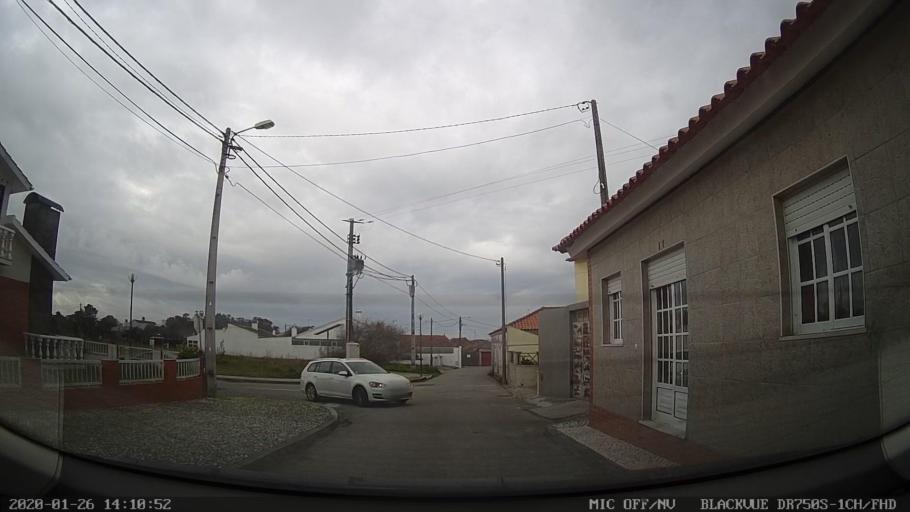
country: PT
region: Aveiro
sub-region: Aveiro
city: Aradas
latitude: 40.6300
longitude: -8.6265
